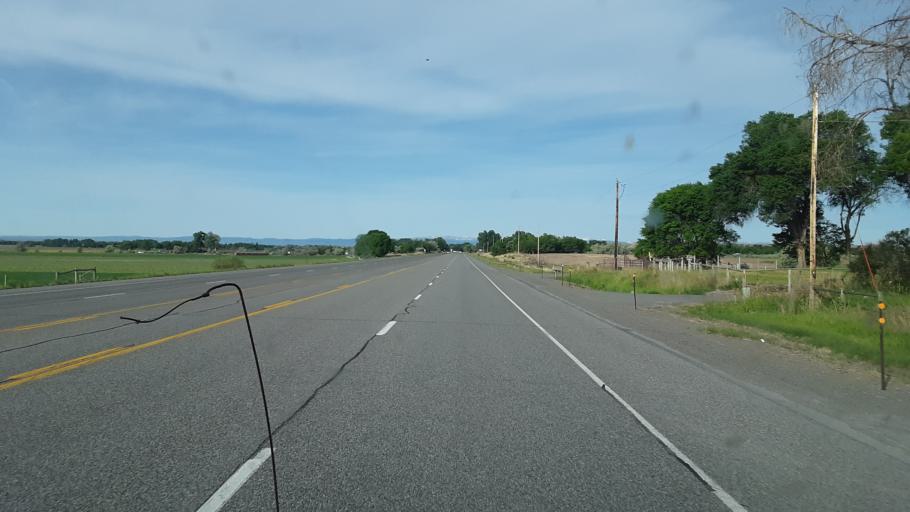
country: US
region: Wyoming
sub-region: Fremont County
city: Riverton
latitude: 43.0925
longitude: -108.3657
